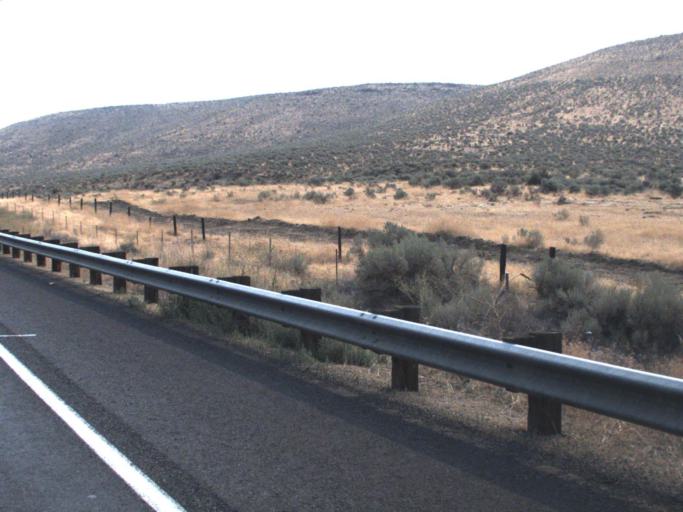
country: US
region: Washington
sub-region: Yakima County
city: Toppenish
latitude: 46.2187
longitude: -120.4387
